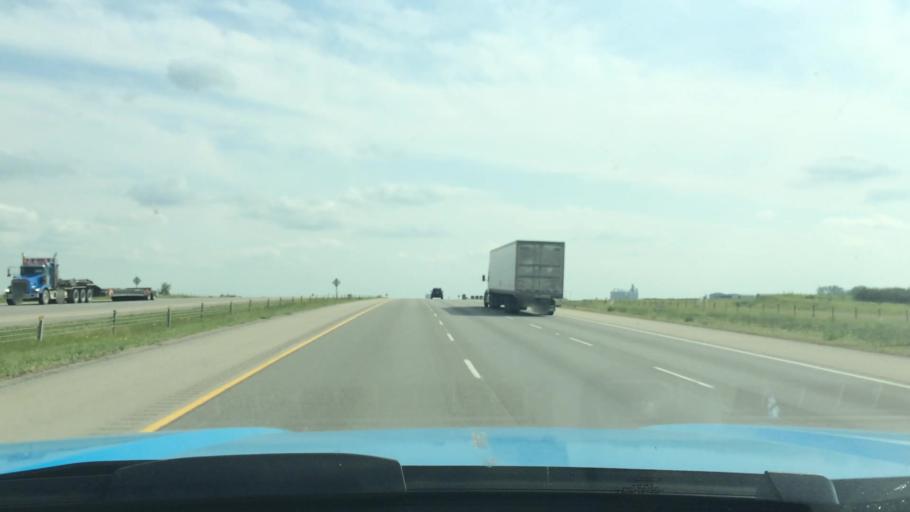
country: CA
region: Alberta
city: Crossfield
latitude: 51.5127
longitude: -114.0252
